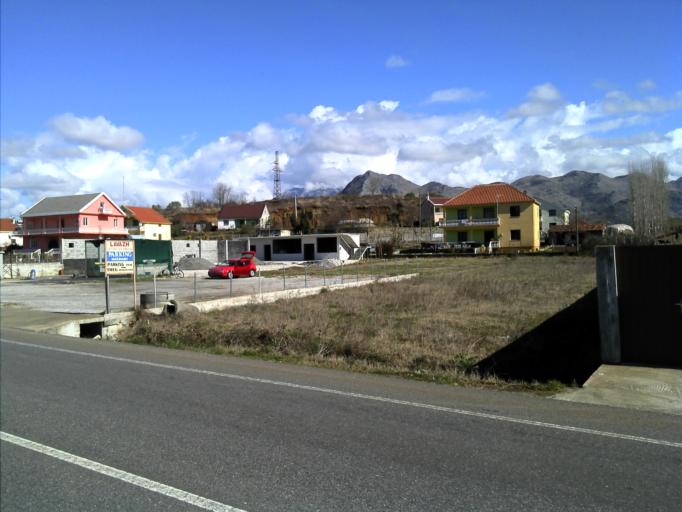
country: AL
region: Shkoder
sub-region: Rrethi i Malesia e Madhe
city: Koplik
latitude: 42.1833
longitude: 19.4594
